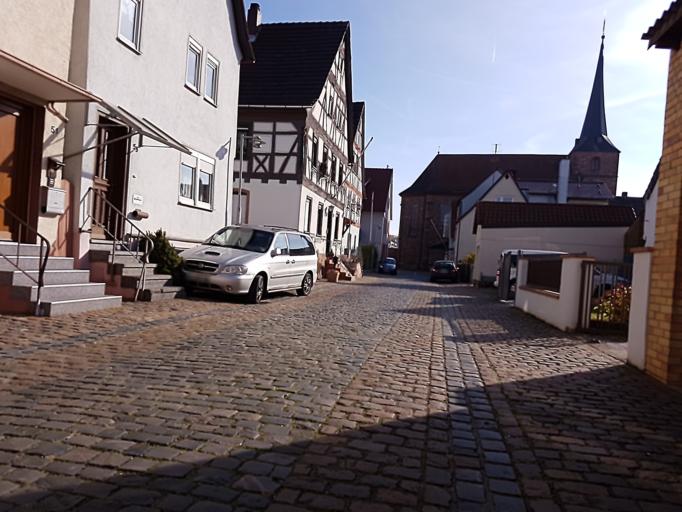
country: DE
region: Bavaria
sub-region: Regierungsbezirk Unterfranken
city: Worth am Main
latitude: 49.7976
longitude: 9.1582
